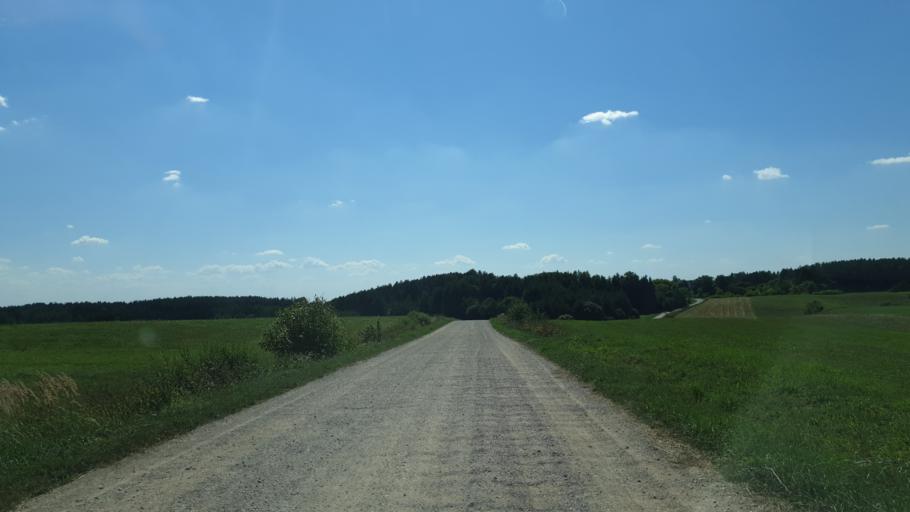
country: LT
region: Vilnius County
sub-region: Vilniaus Rajonas
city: Vievis
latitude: 54.8945
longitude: 24.8645
